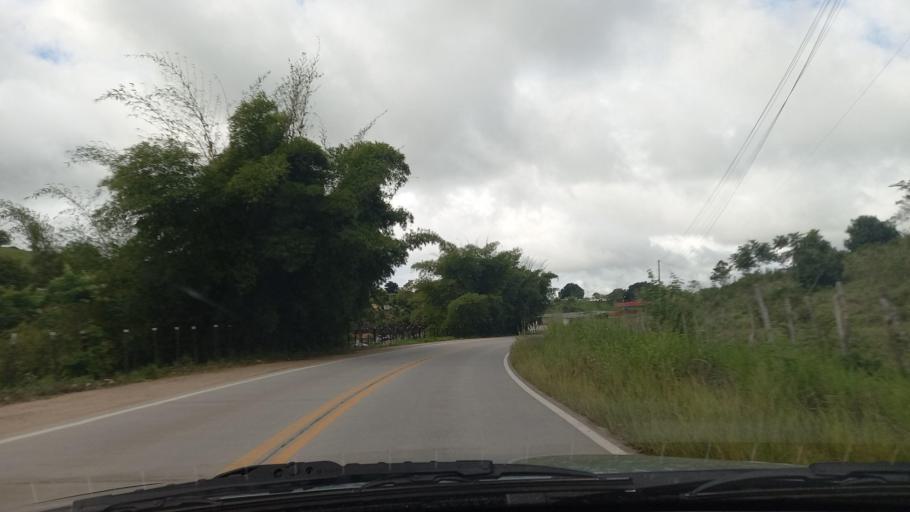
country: BR
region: Pernambuco
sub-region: Quipapa
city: Quipapa
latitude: -8.7867
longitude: -35.9612
